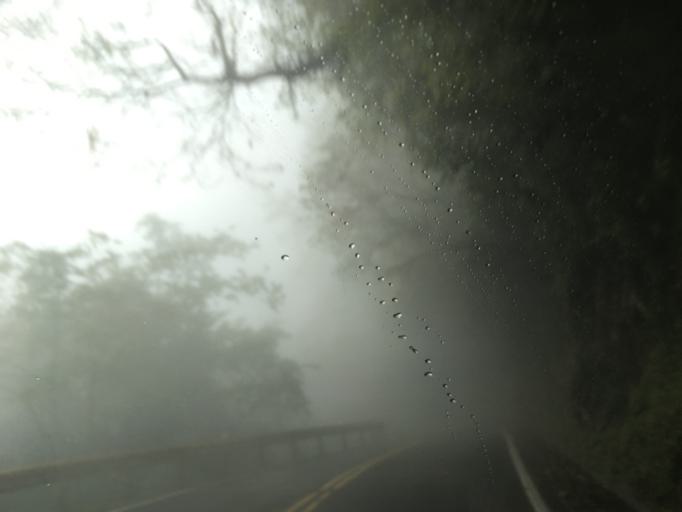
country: TW
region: Taiwan
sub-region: Hualien
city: Hualian
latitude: 24.1896
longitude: 121.4203
